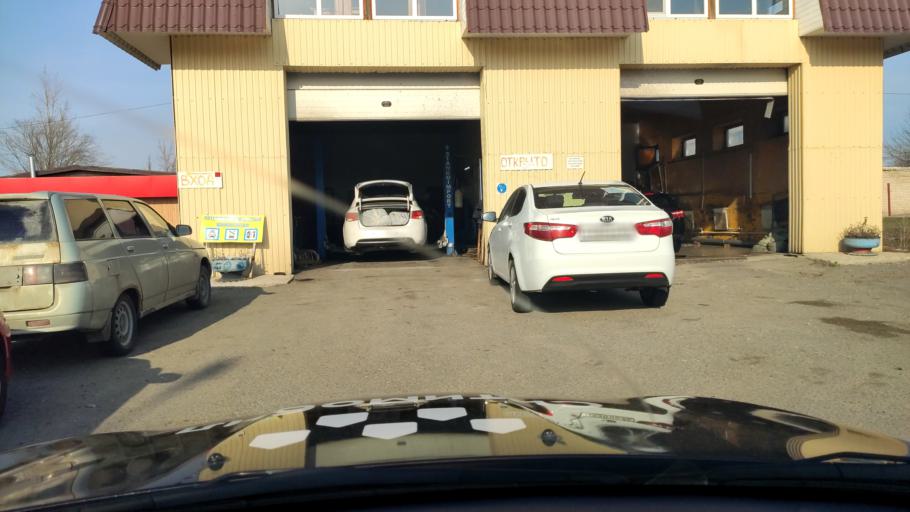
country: RU
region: Samara
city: Povolzhskiy
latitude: 53.5848
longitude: 49.7679
